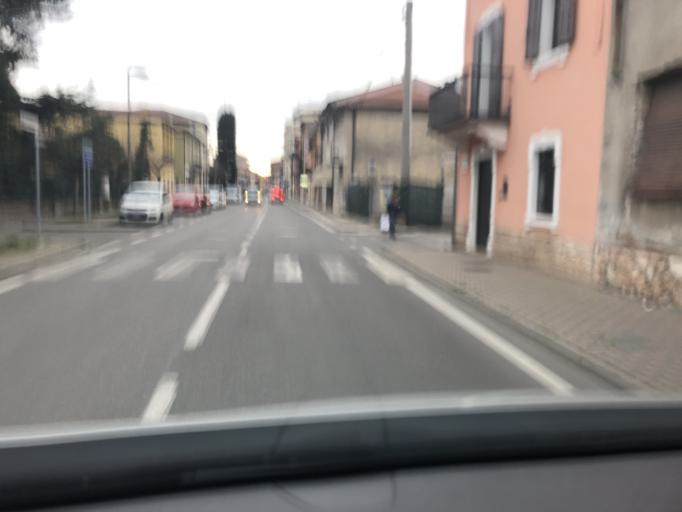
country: IT
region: Veneto
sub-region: Provincia di Verona
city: Lugagnano
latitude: 45.4338
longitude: 10.8942
